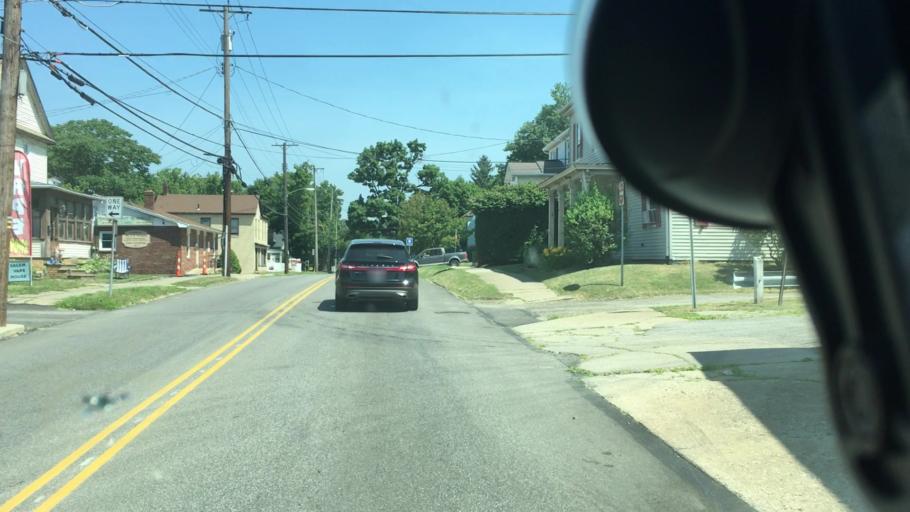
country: US
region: Ohio
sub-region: Columbiana County
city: Salem
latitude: 40.9026
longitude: -80.8567
